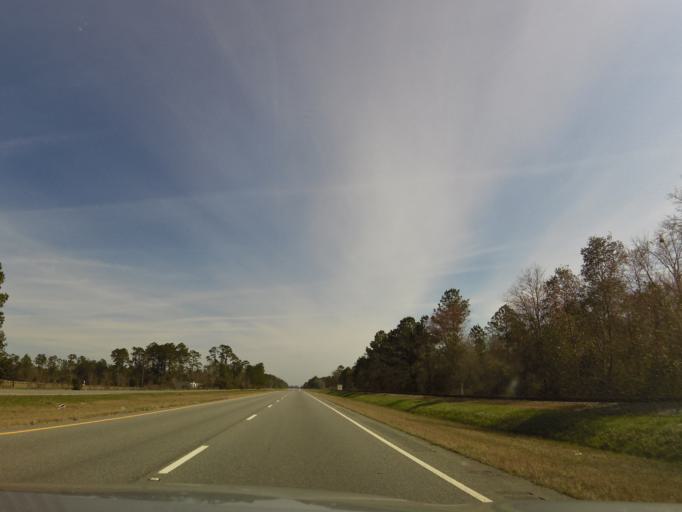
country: US
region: Georgia
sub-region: Lanier County
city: Lakeland
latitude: 30.8904
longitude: -83.1241
